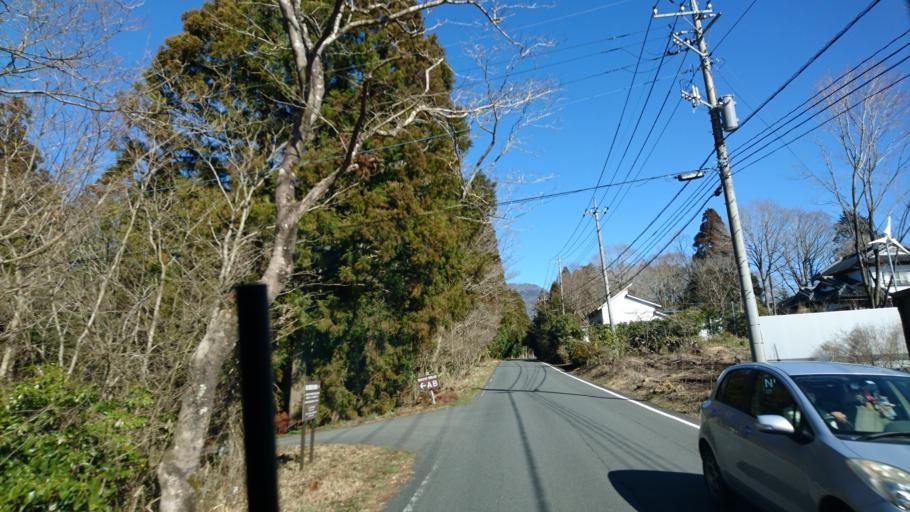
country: JP
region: Shizuoka
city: Fujinomiya
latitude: 35.3477
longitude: 138.5729
